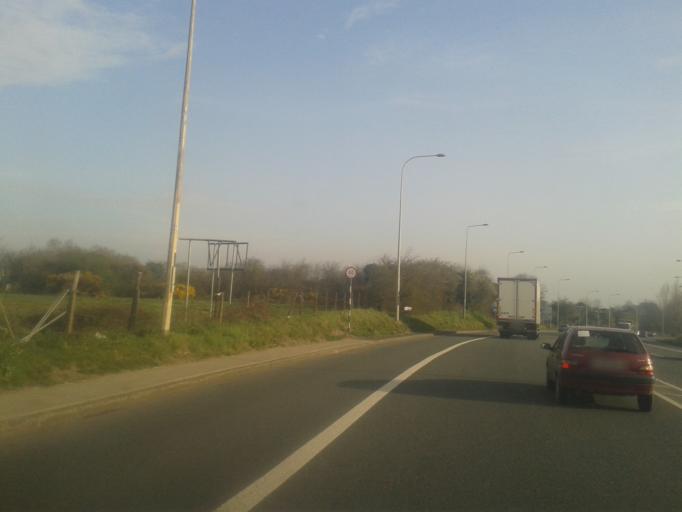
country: IE
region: Leinster
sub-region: Fingal County
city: Swords
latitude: 53.4470
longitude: -6.2282
